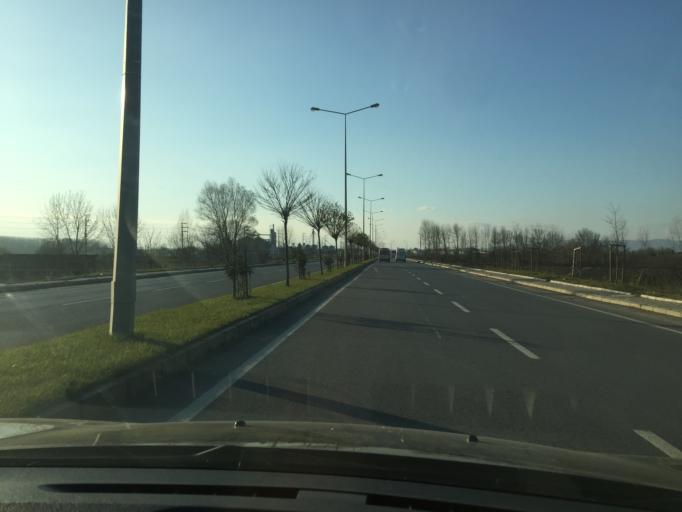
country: TR
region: Sakarya
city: Sogutlu
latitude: 40.9037
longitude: 30.4934
